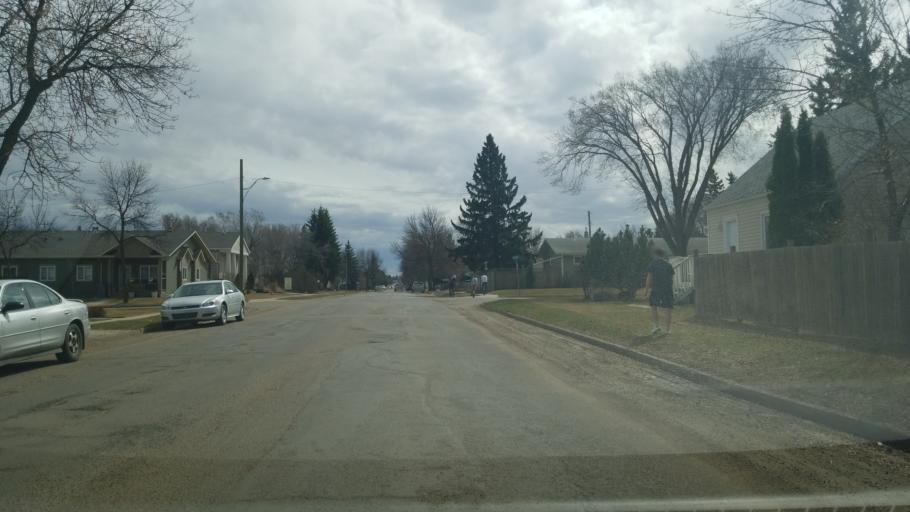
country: CA
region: Saskatchewan
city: Lloydminster
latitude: 53.2756
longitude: -110.0036
